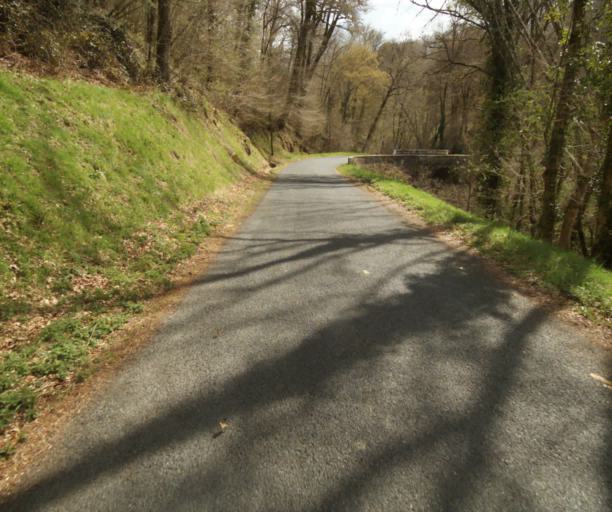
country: FR
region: Limousin
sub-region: Departement de la Correze
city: Laguenne
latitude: 45.2514
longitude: 1.8879
